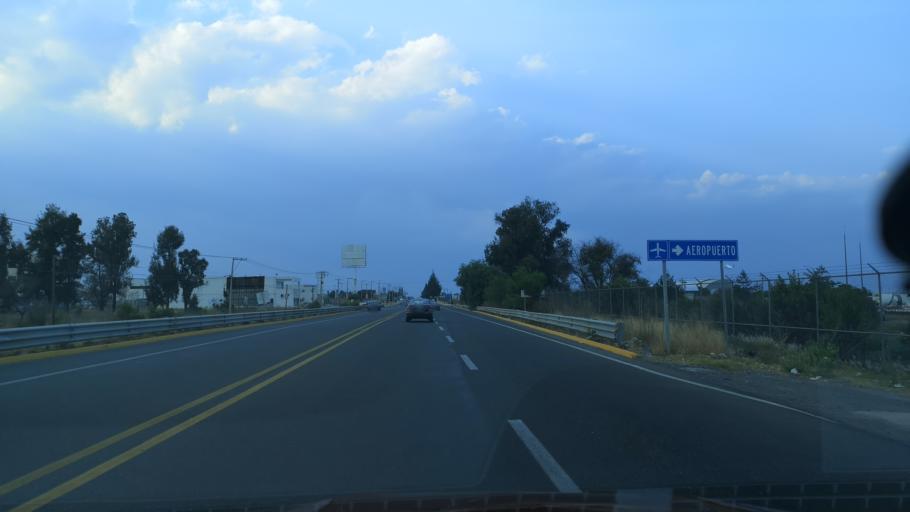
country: MX
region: Puebla
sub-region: Huejotzingo
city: Los Encinos
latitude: 19.1588
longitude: -98.3772
